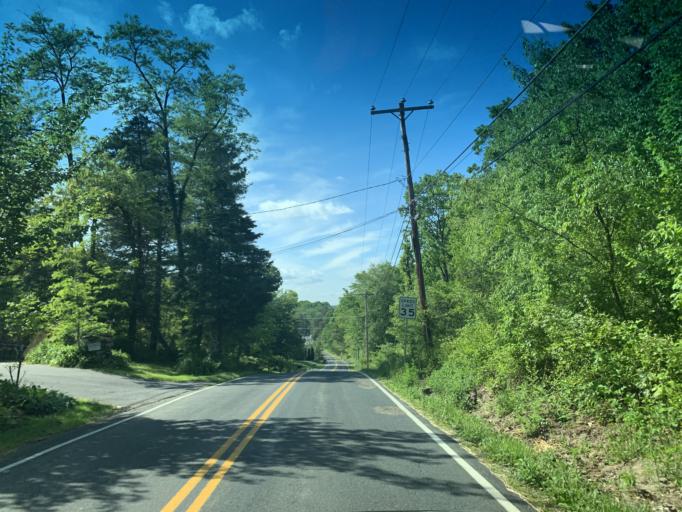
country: US
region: Maryland
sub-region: Cecil County
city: Rising Sun
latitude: 39.7062
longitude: -76.1809
